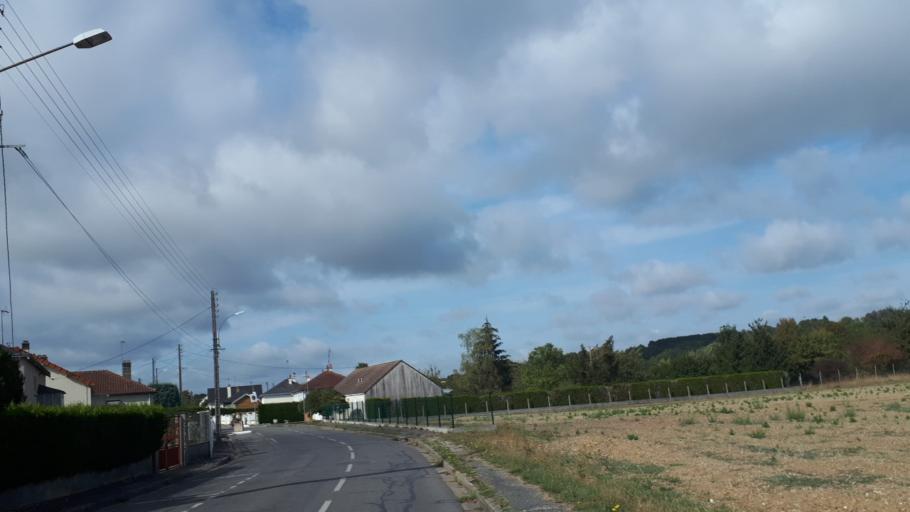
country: FR
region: Centre
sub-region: Departement du Loir-et-Cher
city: Naveil
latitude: 47.7954
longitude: 1.0377
